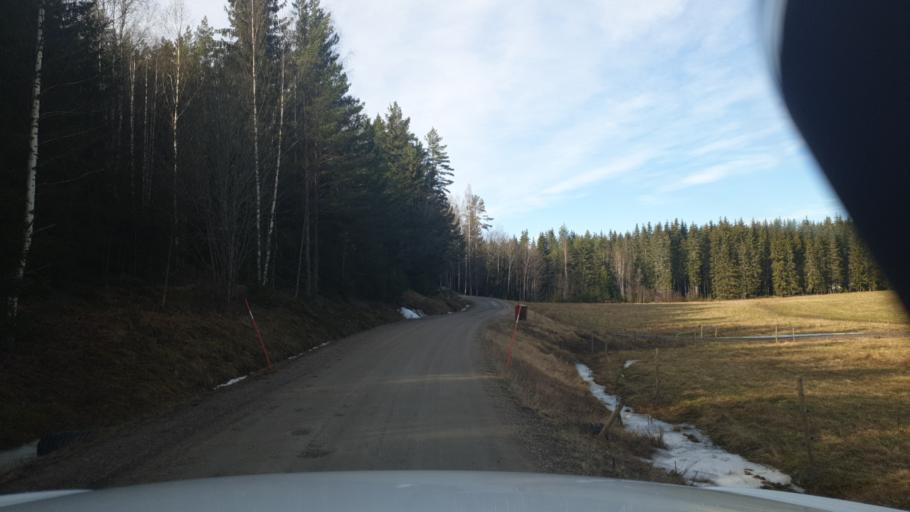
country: SE
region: Vaermland
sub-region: Arvika Kommun
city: Arvika
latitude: 59.6006
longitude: 12.7882
